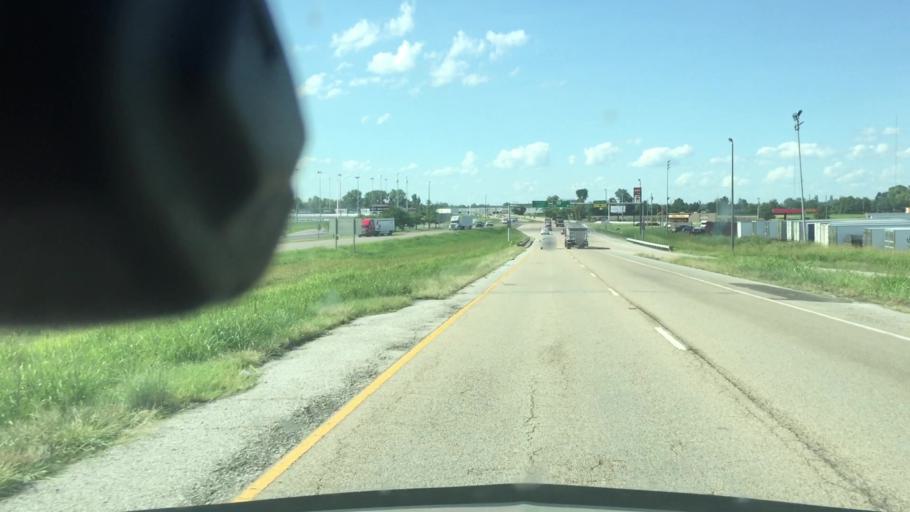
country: US
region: Illinois
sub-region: Saint Clair County
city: East Saint Louis
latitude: 38.6492
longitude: -90.1321
